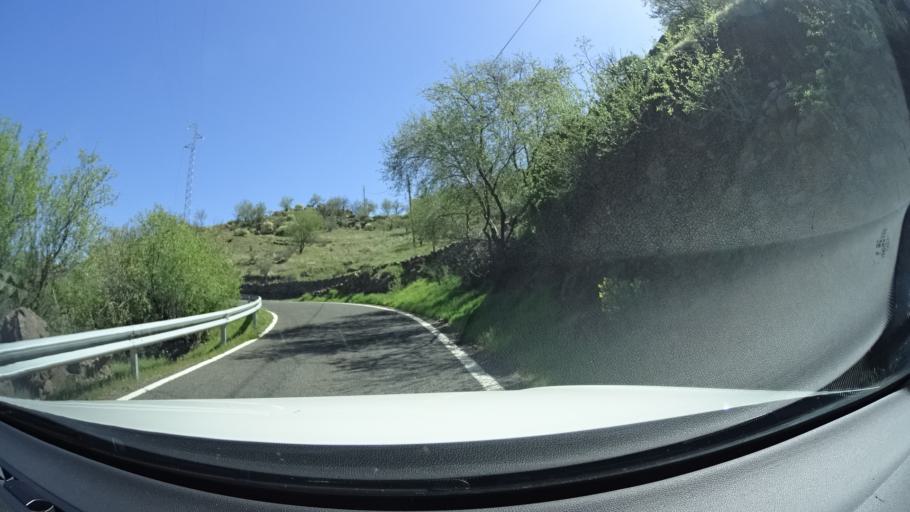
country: ES
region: Canary Islands
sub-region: Provincia de Las Palmas
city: Tejeda
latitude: 27.9890
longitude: -15.6338
